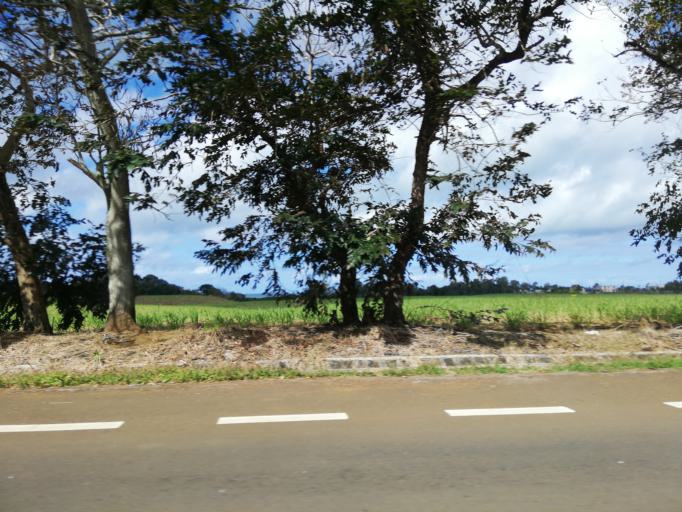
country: MU
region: Grand Port
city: Mahebourg
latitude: -20.3847
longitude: 57.6969
